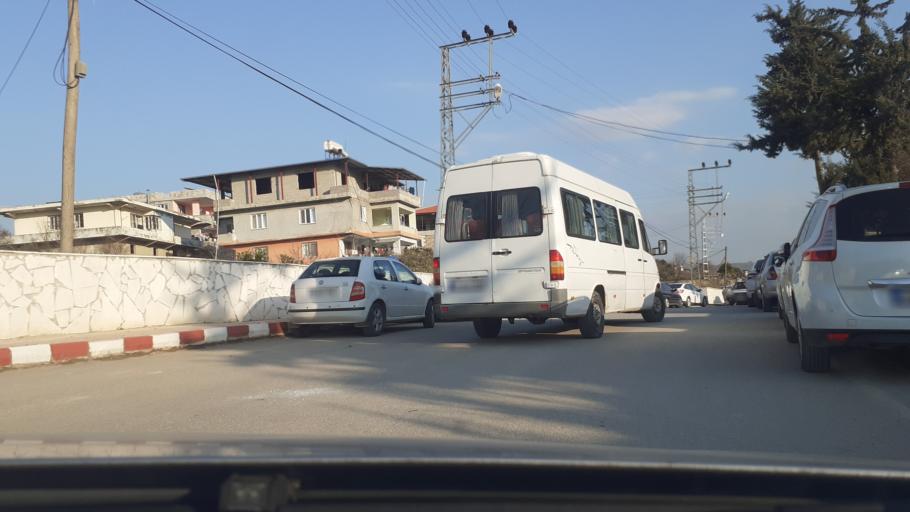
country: TR
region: Hatay
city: Fatikli
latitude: 36.1142
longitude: 36.2640
